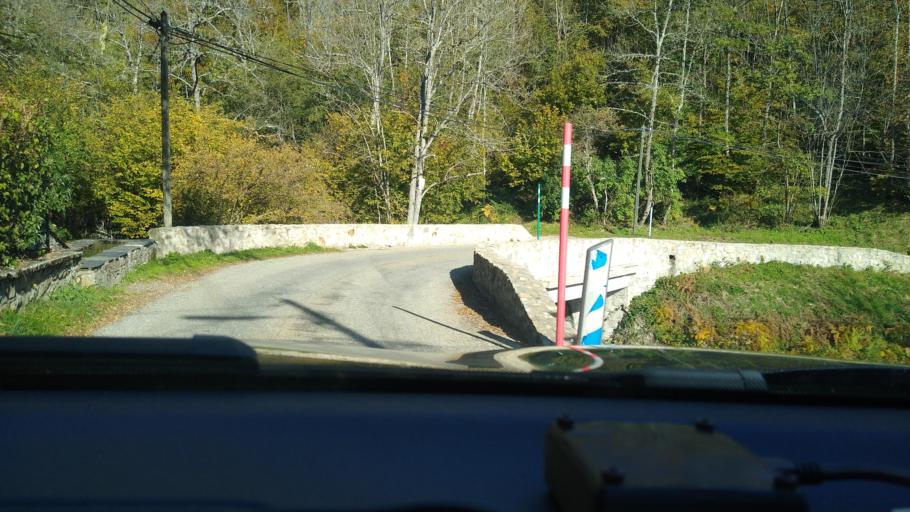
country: FR
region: Midi-Pyrenees
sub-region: Departement de l'Ariege
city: Ax-les-Thermes
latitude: 42.7255
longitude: 1.8891
